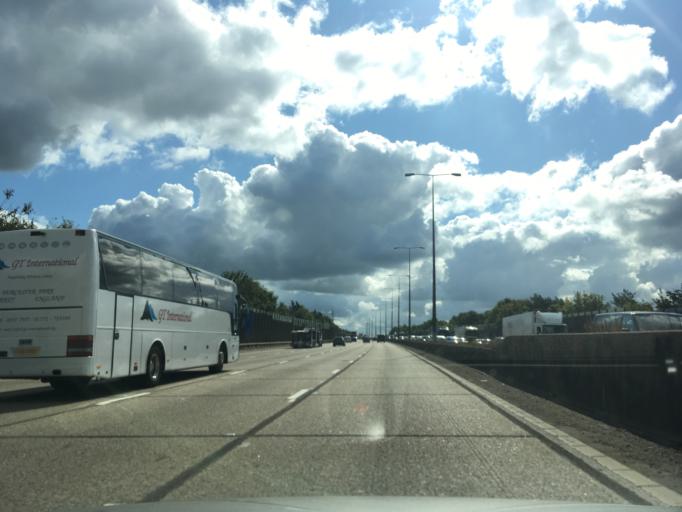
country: GB
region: England
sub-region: Surrey
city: Addlestone
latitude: 51.3550
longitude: -0.4923
